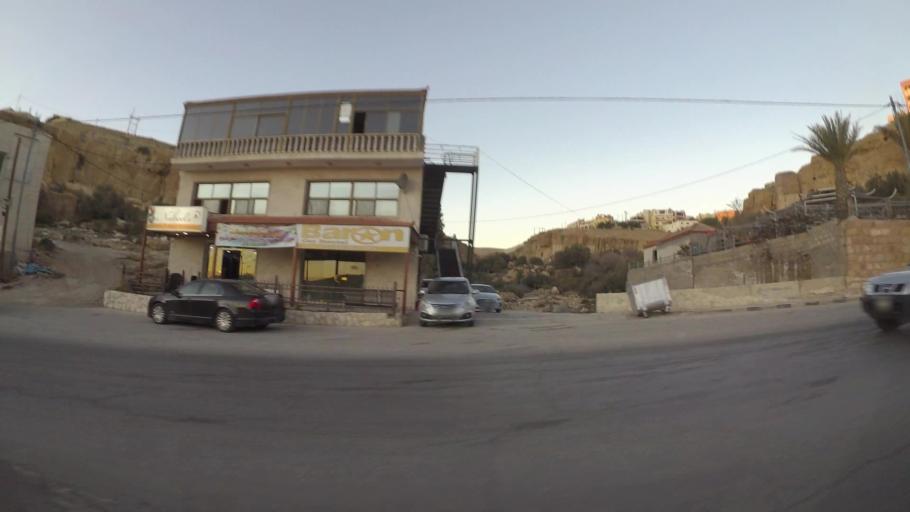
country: JO
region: Ma'an
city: Petra
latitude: 30.3260
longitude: 35.4748
